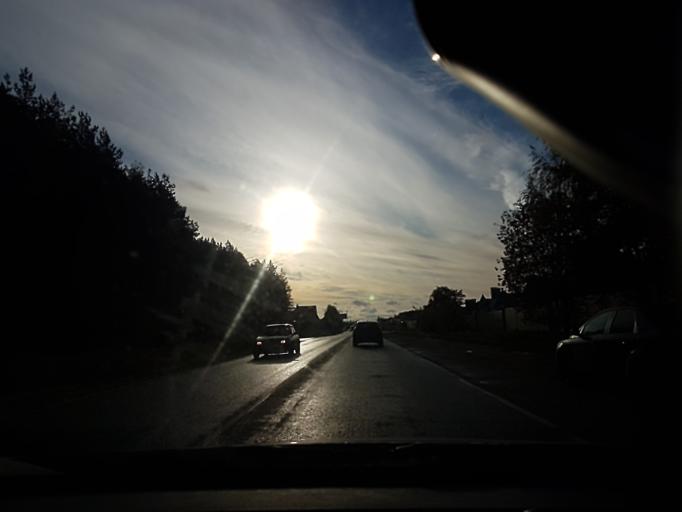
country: RU
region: Moskovskaya
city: Rozhdestveno
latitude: 55.8254
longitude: 37.0419
